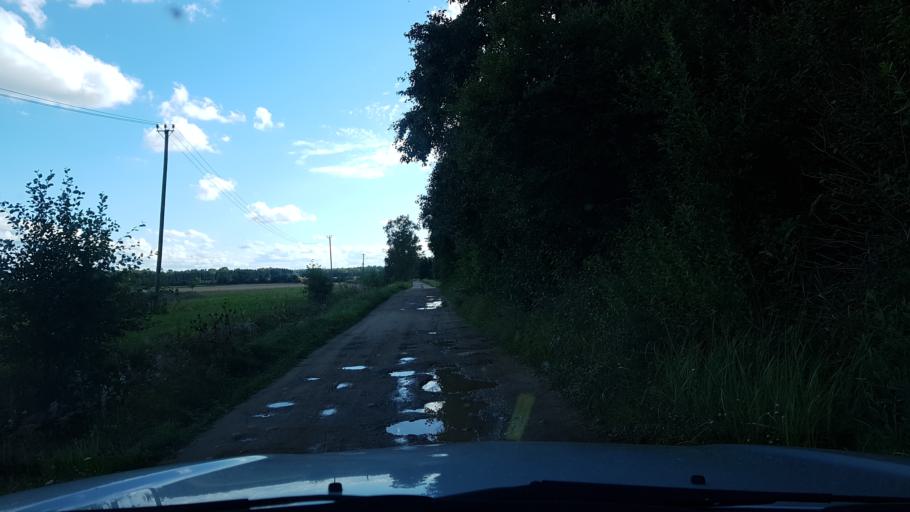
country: EE
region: Harju
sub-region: Rae vald
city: Jueri
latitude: 59.3623
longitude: 24.8584
